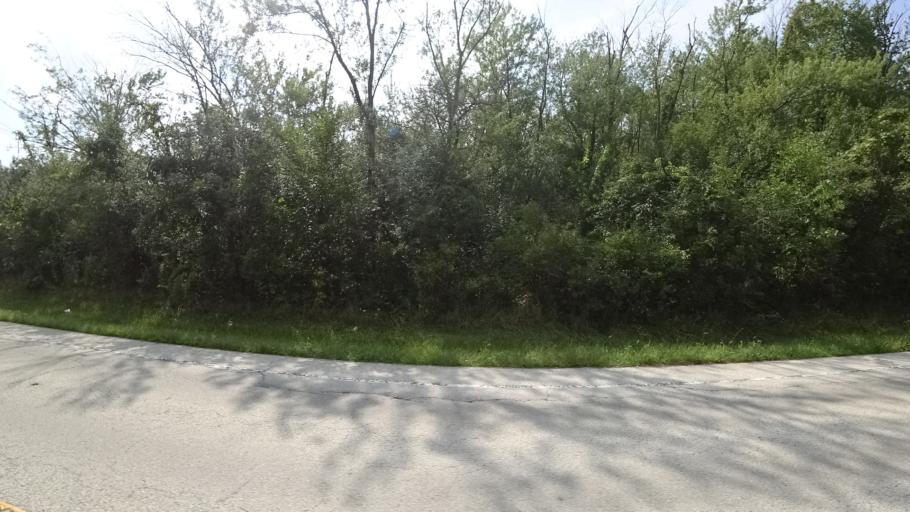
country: US
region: Illinois
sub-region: Will County
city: Goodings Grove
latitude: 41.6564
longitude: -87.9123
